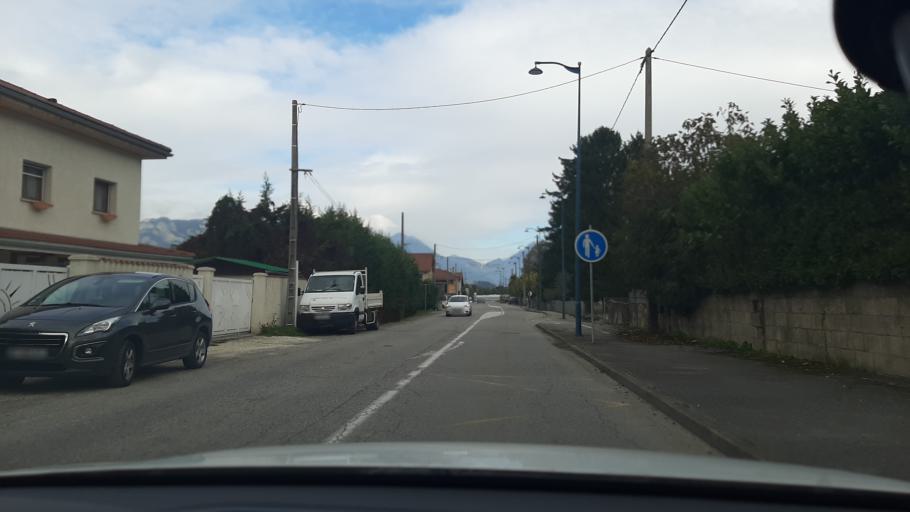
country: FR
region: Rhone-Alpes
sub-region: Departement de l'Isere
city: Pontcharra
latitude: 45.4398
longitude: 6.0294
